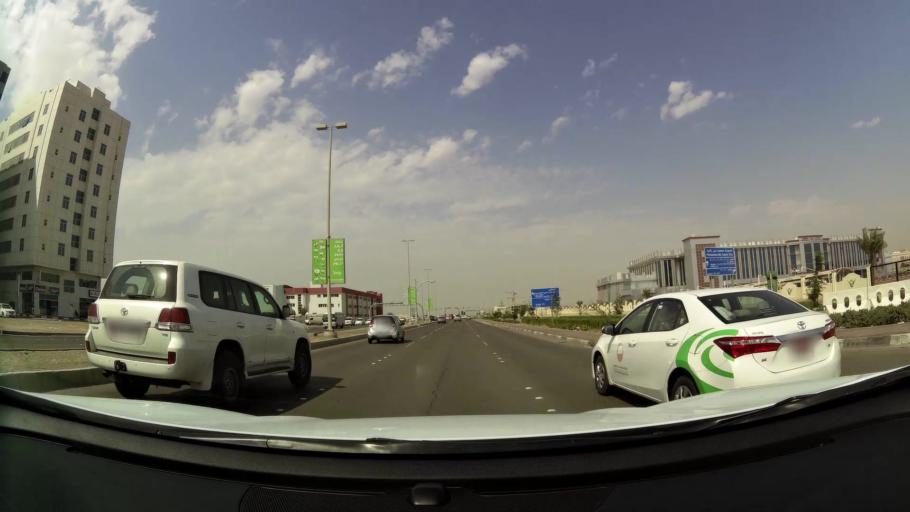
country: AE
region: Abu Dhabi
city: Abu Dhabi
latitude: 24.3446
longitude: 54.5380
